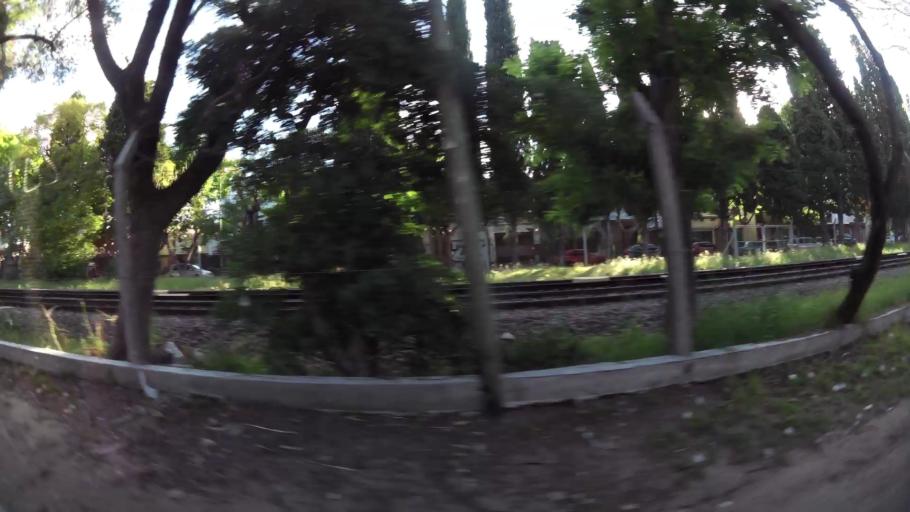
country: AR
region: Buenos Aires
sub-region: Partido de General San Martin
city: General San Martin
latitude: -34.5538
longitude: -58.5524
